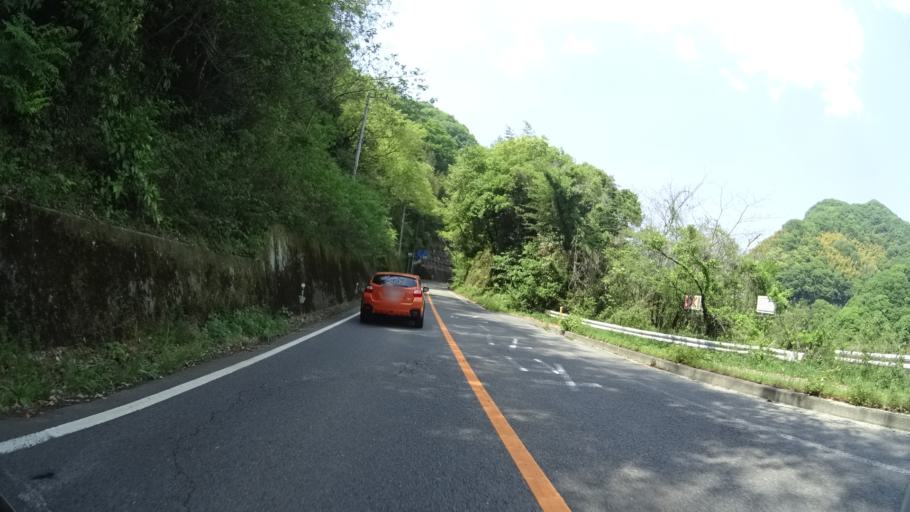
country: JP
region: Ehime
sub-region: Shikoku-chuo Shi
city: Matsuyama
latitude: 33.8875
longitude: 132.8368
